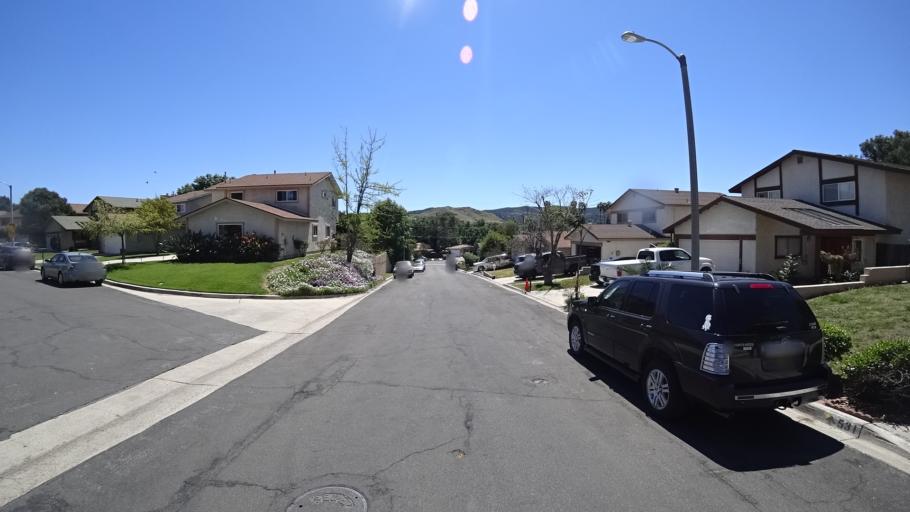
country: US
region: California
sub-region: Ventura County
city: Thousand Oaks
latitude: 34.1845
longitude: -118.8653
